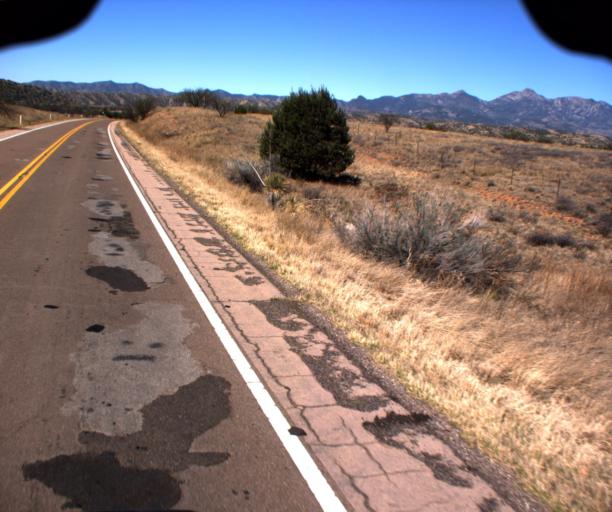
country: US
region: Arizona
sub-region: Pima County
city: Corona de Tucson
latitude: 31.6620
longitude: -110.6856
